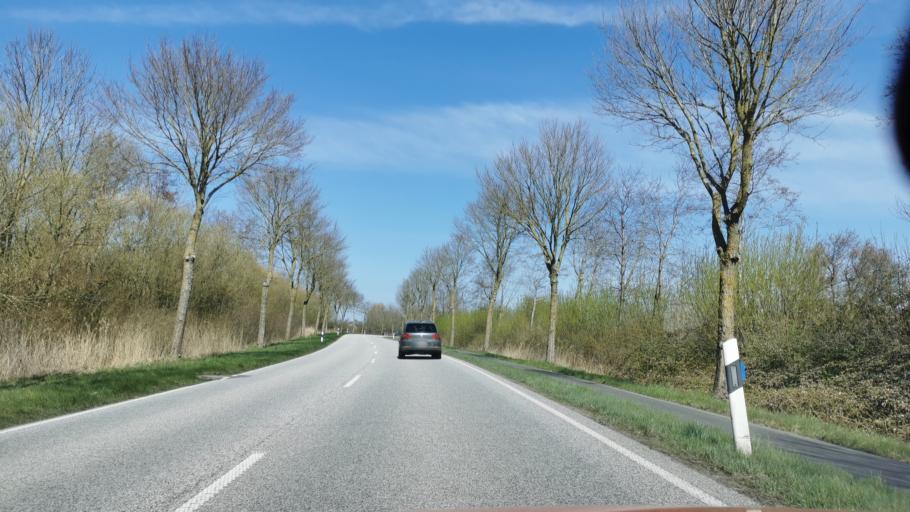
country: DE
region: Schleswig-Holstein
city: Friedrichsgabekoog
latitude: 54.1614
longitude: 8.9724
